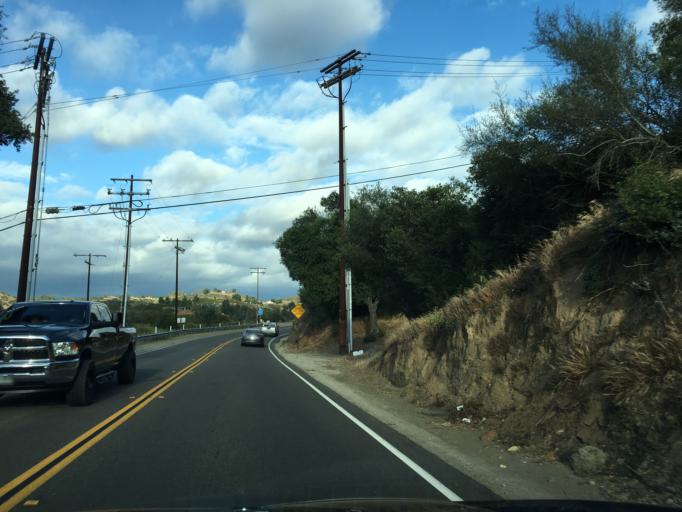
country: US
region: California
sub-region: San Diego County
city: Valley Center
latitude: 33.2496
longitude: -117.0589
